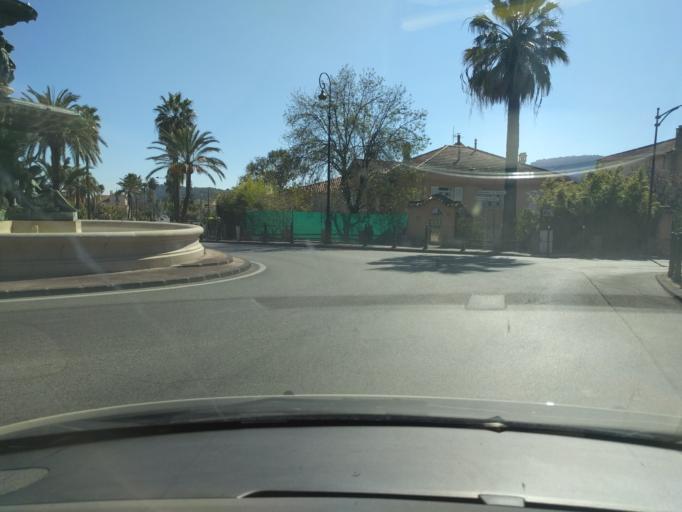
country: FR
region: Provence-Alpes-Cote d'Azur
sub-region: Departement du Var
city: Hyeres
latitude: 43.1179
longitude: 6.1224
